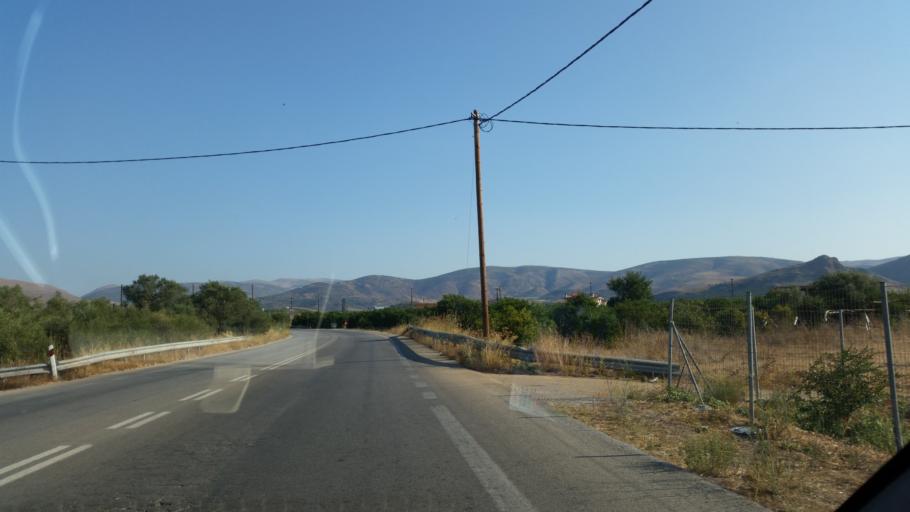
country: GR
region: Peloponnese
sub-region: Nomos Argolidos
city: Ayia Trias
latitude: 37.6307
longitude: 22.8171
